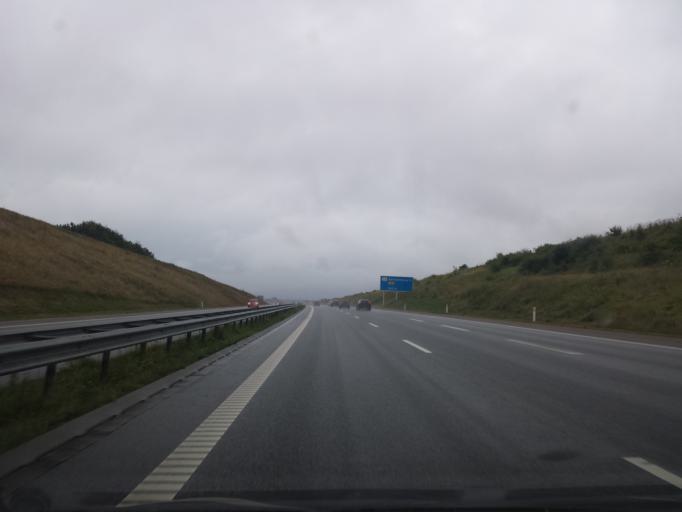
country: DK
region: South Denmark
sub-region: Sonderborg Kommune
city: Dybbol
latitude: 54.9217
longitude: 9.7343
